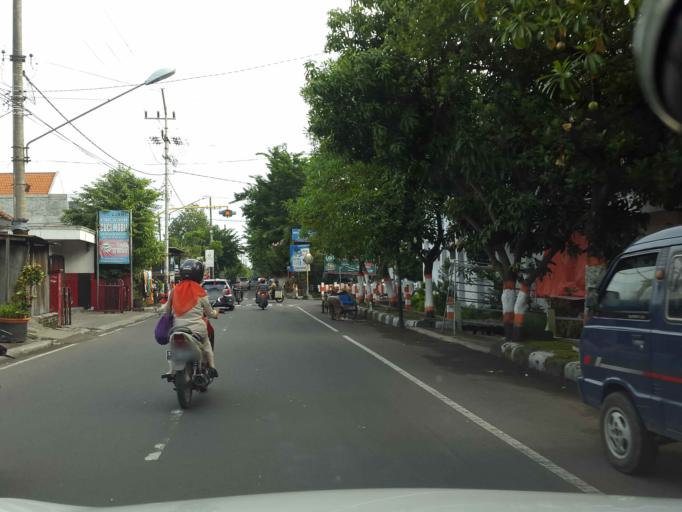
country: ID
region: East Java
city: Mojokerto
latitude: -7.4723
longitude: 112.4293
